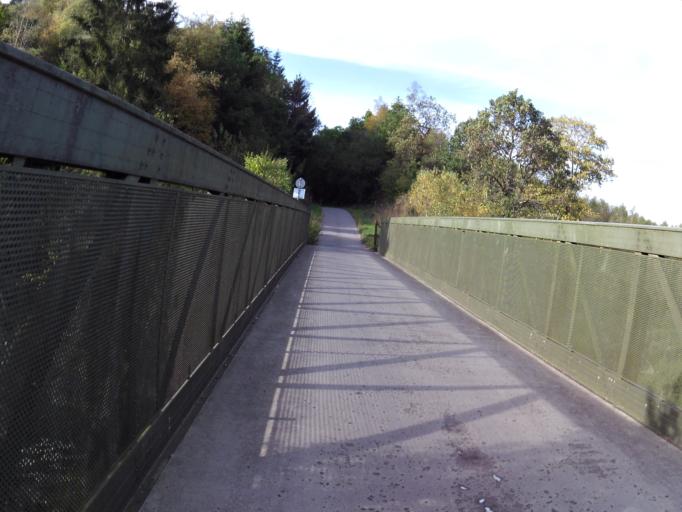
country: BE
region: Wallonia
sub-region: Province de Liege
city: Saint-Vith
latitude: 50.2439
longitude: 6.1539
